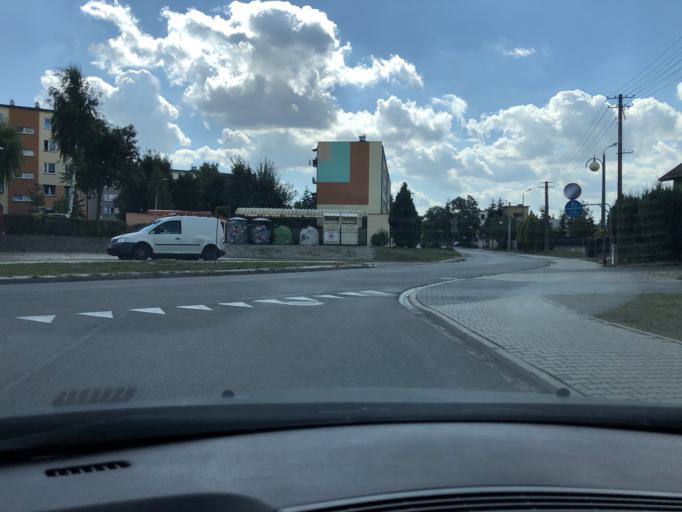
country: PL
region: Lodz Voivodeship
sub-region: Powiat wieruszowski
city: Wieruszow
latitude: 51.2981
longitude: 18.1611
